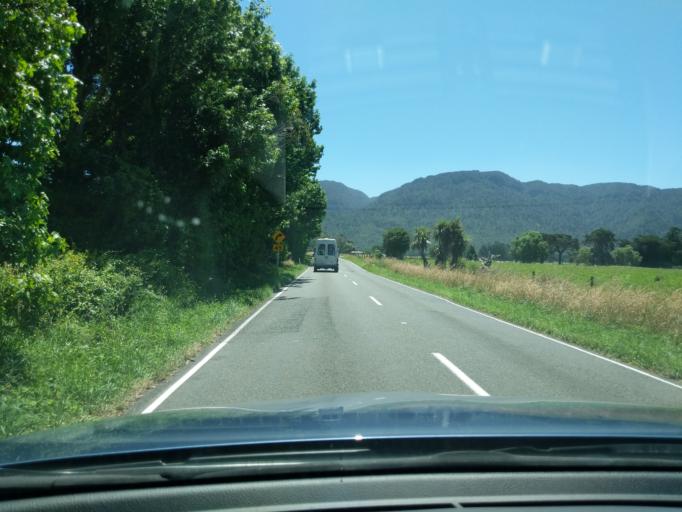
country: NZ
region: Tasman
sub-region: Tasman District
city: Takaka
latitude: -40.7024
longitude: 172.6336
